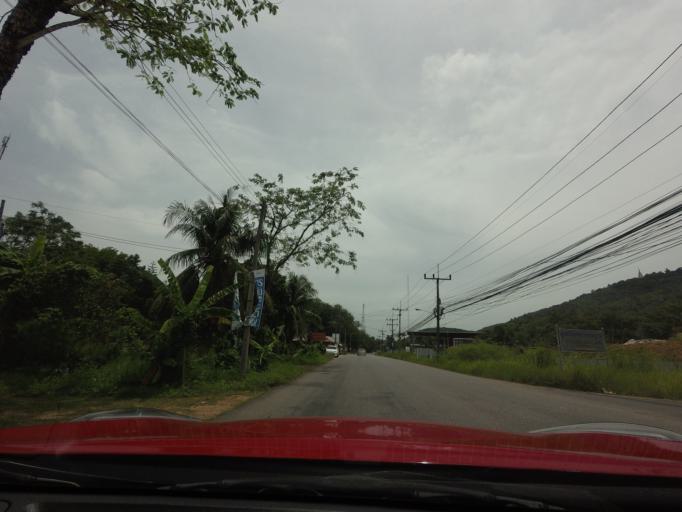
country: TH
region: Songkhla
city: Hat Yai
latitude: 7.0010
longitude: 100.5244
